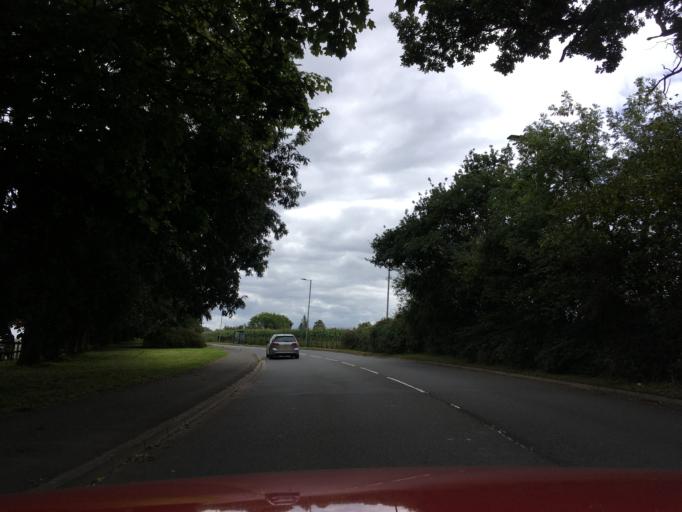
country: GB
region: England
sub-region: Devon
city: Cullompton
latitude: 50.8671
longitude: -3.3916
